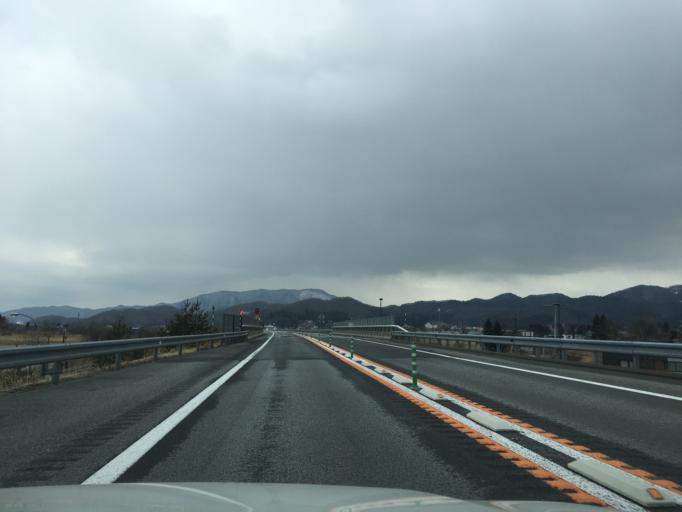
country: JP
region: Aomori
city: Aomori Shi
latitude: 40.7989
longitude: 140.7846
